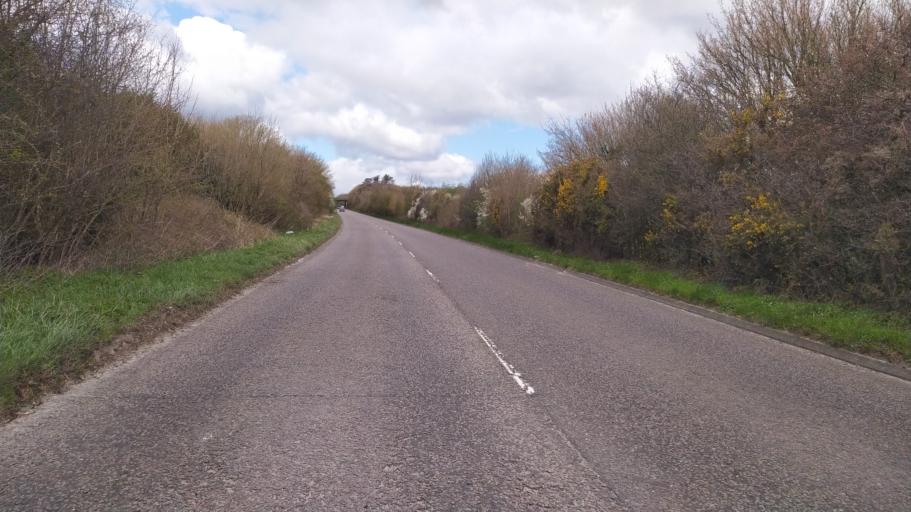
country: GB
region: England
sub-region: Wiltshire
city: Chicklade
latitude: 51.1011
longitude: -2.1628
